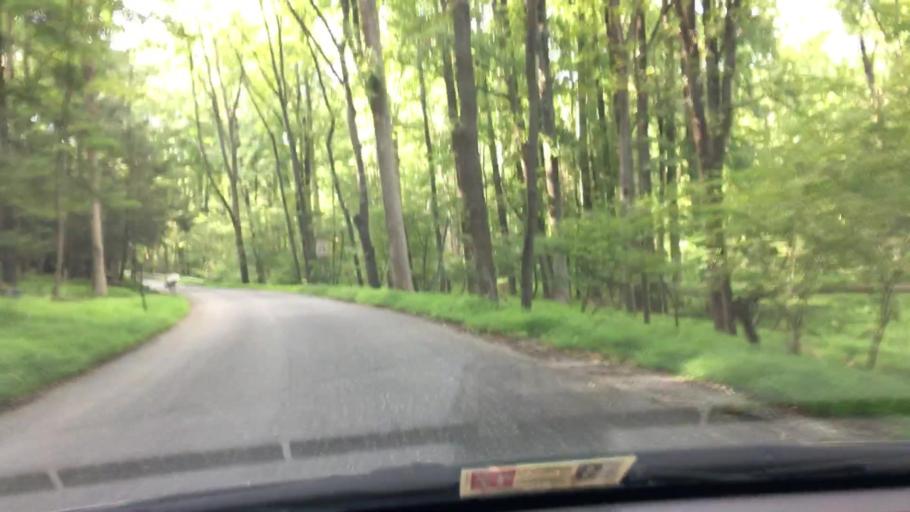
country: US
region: Maryland
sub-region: Montgomery County
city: Montgomery Village
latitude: 39.2151
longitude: -77.2098
